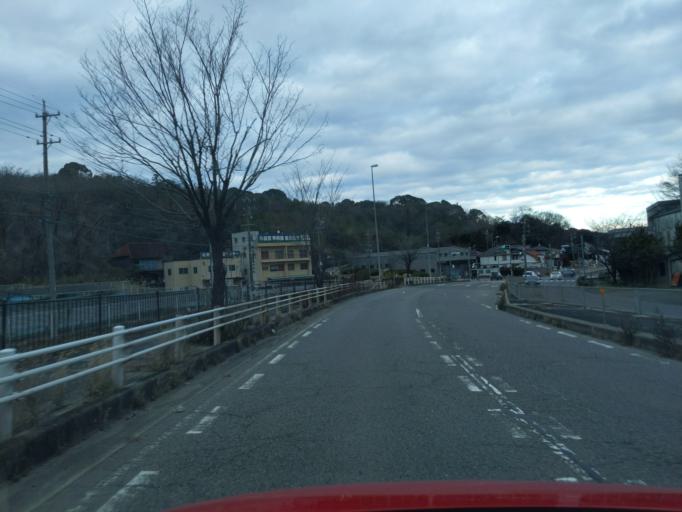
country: JP
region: Gifu
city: Tajimi
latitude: 35.3321
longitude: 137.0976
